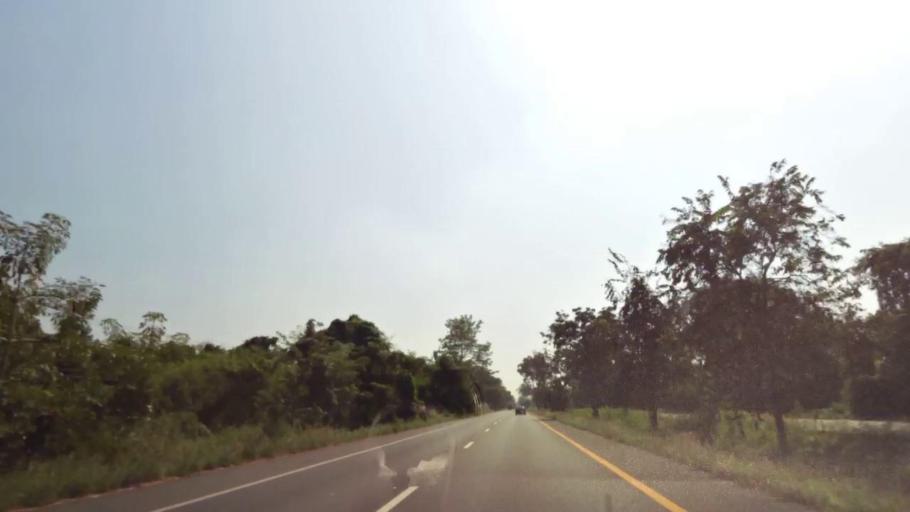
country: TH
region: Nakhon Sawan
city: Banphot Phisai
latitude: 16.0016
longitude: 100.1162
